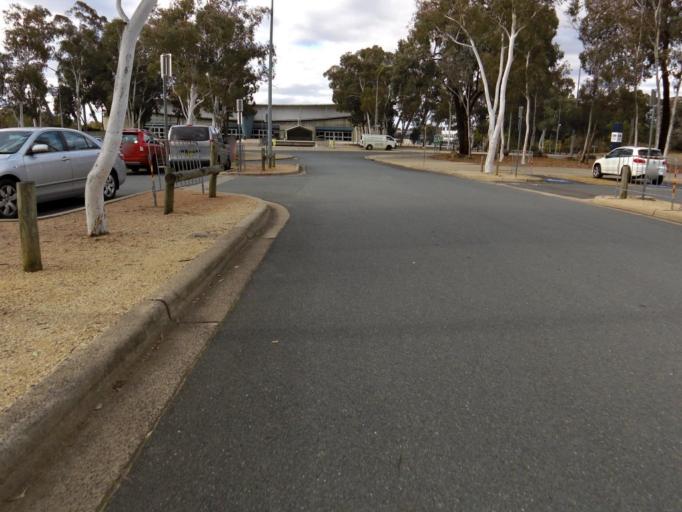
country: AU
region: Australian Capital Territory
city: Kaleen
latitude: -35.2491
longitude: 149.1002
